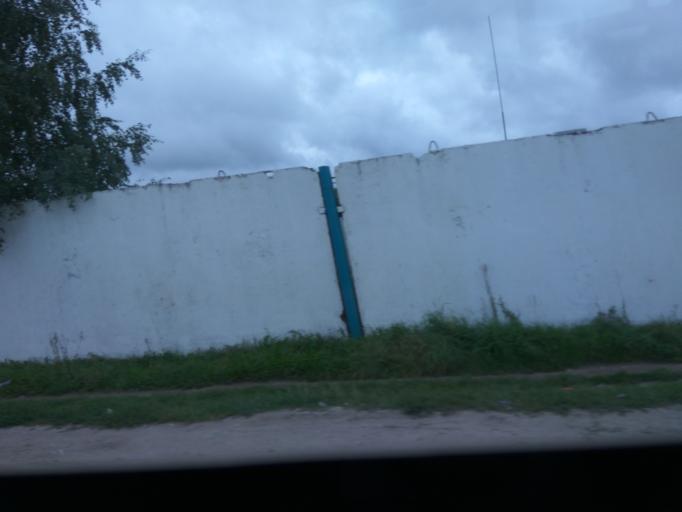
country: RU
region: Moskovskaya
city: Malyshevo
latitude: 55.5143
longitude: 38.3427
